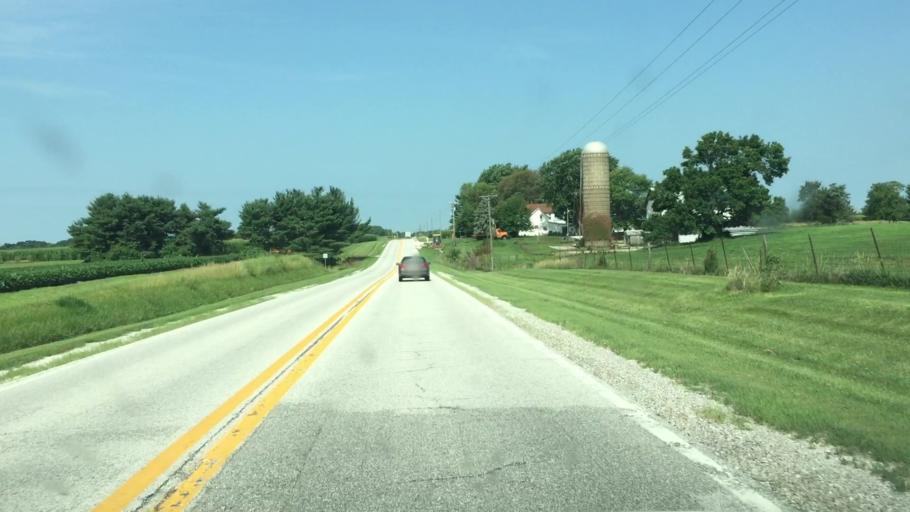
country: US
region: Illinois
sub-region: Hancock County
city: Nauvoo
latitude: 40.5519
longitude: -91.3371
